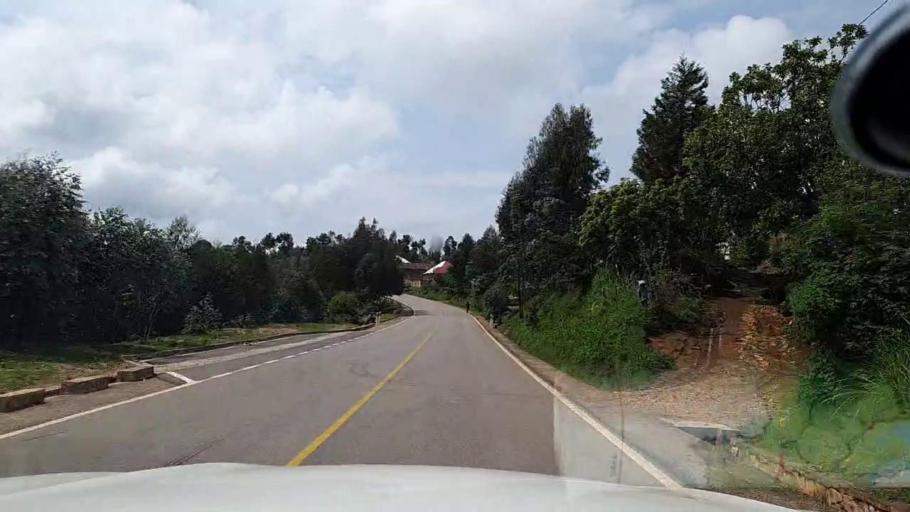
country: RW
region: Southern Province
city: Nzega
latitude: -2.4950
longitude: 29.5067
